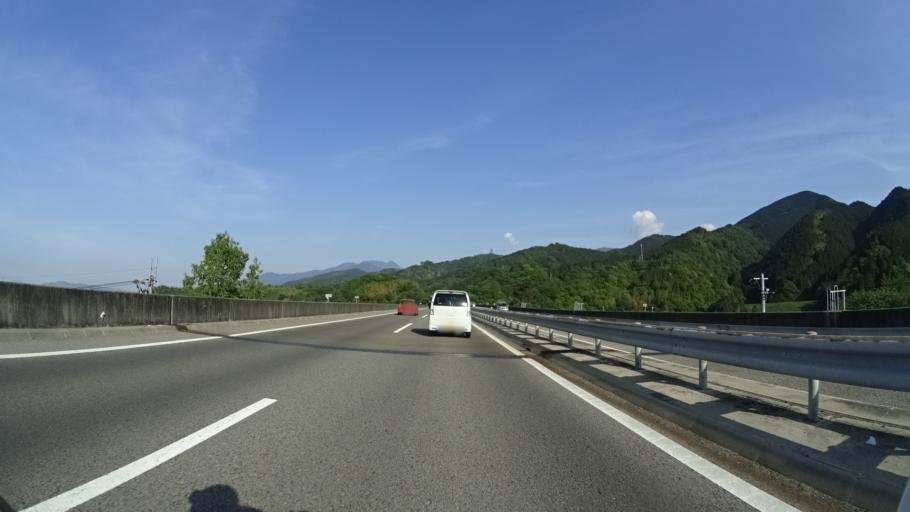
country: JP
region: Ehime
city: Saijo
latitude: 33.8846
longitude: 133.1110
